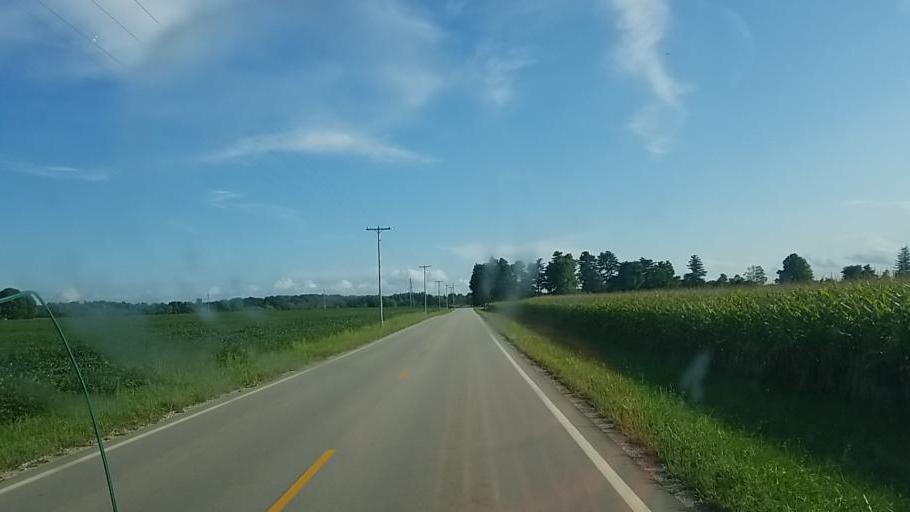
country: US
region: Ohio
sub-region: Wyandot County
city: Upper Sandusky
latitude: 40.8376
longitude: -83.1317
